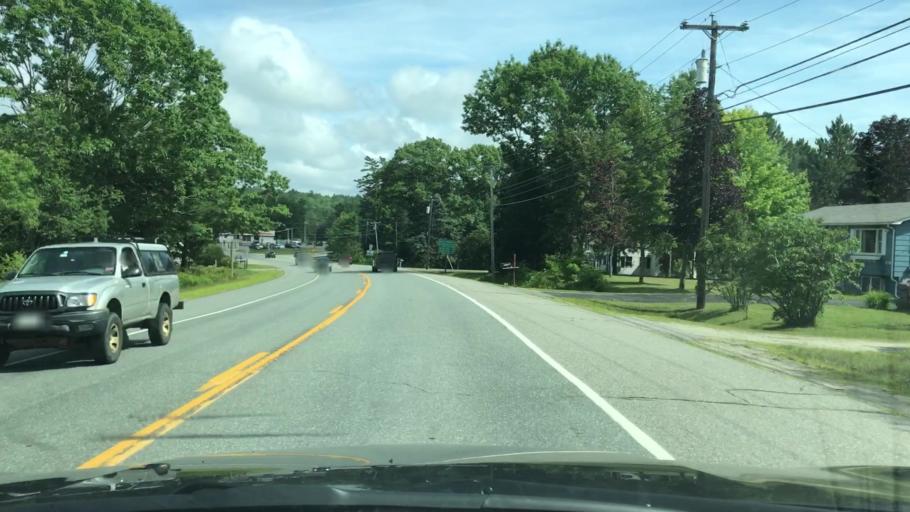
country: US
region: Maine
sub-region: Hancock County
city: Orland
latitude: 44.5614
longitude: -68.7119
